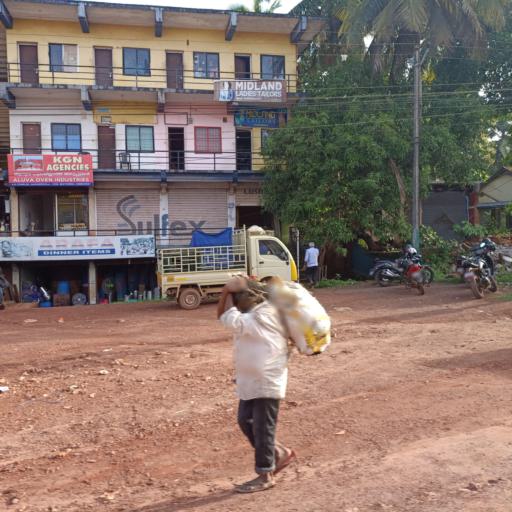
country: IN
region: Kerala
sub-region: Kasaragod District
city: Kasaragod
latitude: 12.5157
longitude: 75.0220
